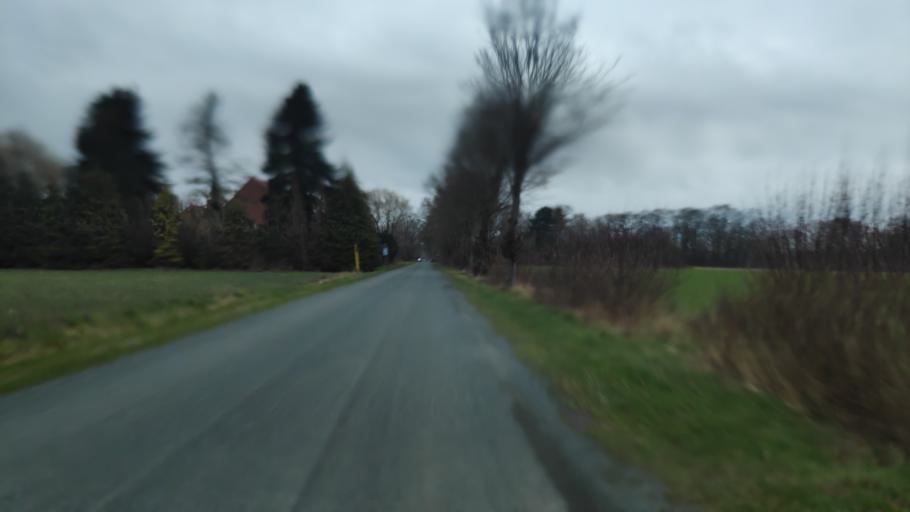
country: DE
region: North Rhine-Westphalia
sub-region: Regierungsbezirk Detmold
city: Hille
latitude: 52.3743
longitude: 8.7738
